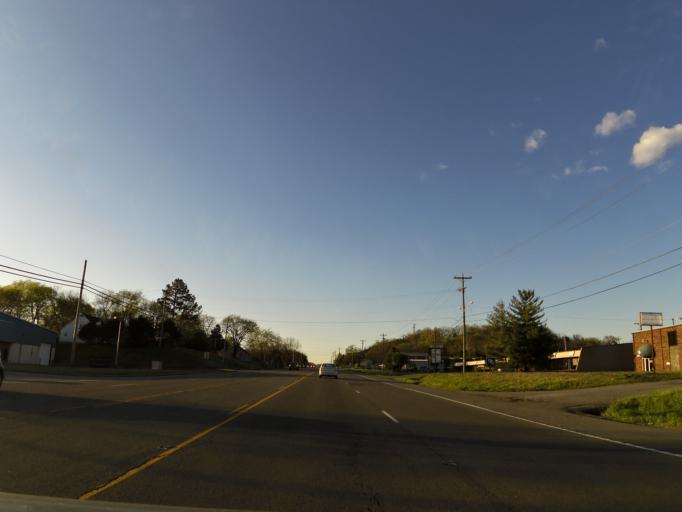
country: US
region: Tennessee
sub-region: Davidson County
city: Goodlettsville
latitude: 36.3446
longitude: -86.7199
